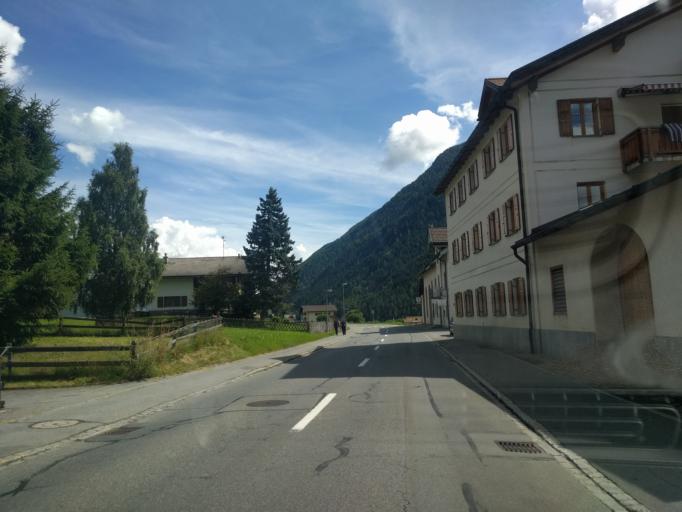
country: IT
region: Trentino-Alto Adige
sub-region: Bolzano
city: Tubre
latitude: 46.6301
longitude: 10.4512
